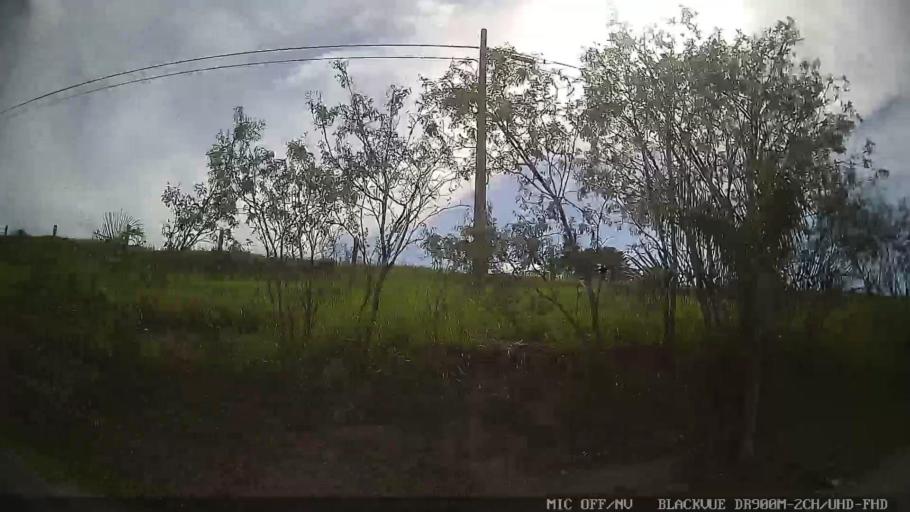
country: BR
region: Sao Paulo
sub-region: Conchas
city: Conchas
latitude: -23.0225
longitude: -47.9978
